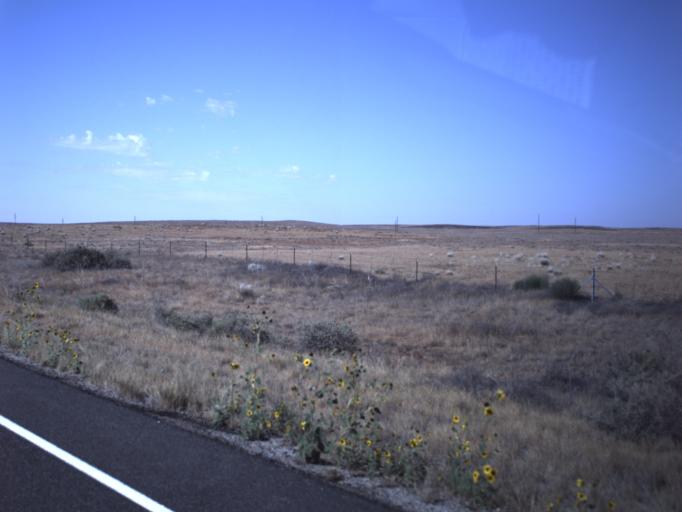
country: US
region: Utah
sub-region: San Juan County
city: Blanding
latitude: 37.4076
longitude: -109.4893
